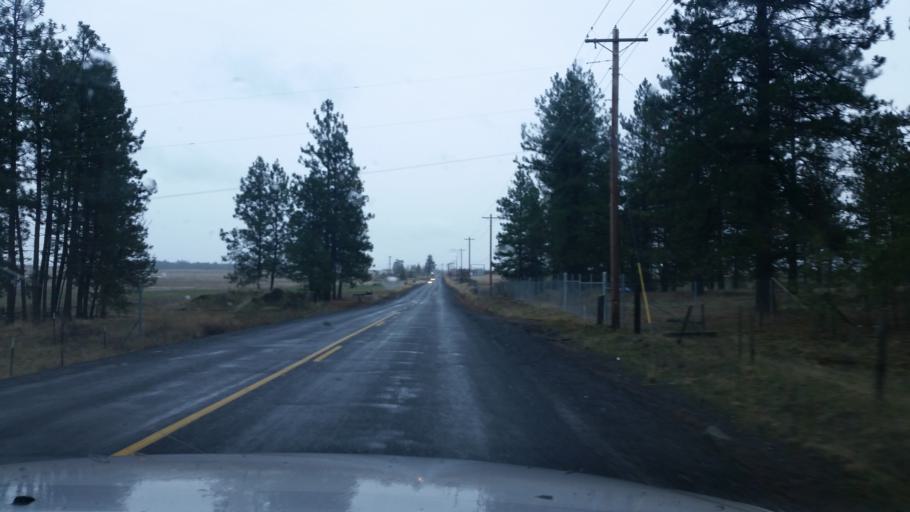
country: US
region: Washington
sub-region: Spokane County
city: Airway Heights
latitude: 47.6719
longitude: -117.5829
